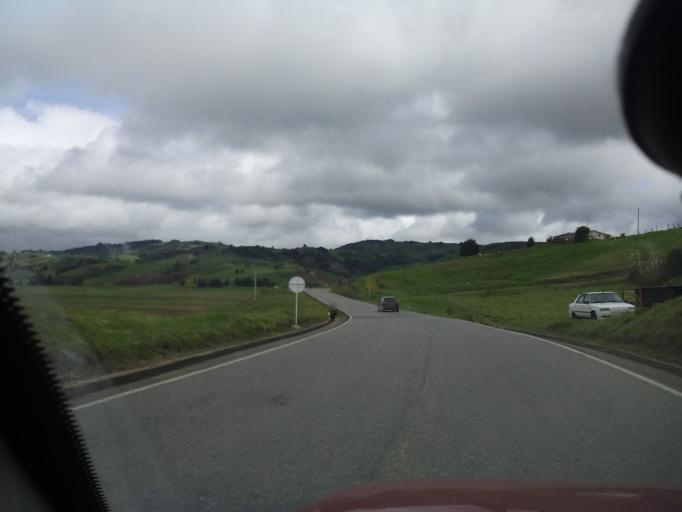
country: CO
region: Boyaca
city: Combita
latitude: 5.6586
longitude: -73.3564
